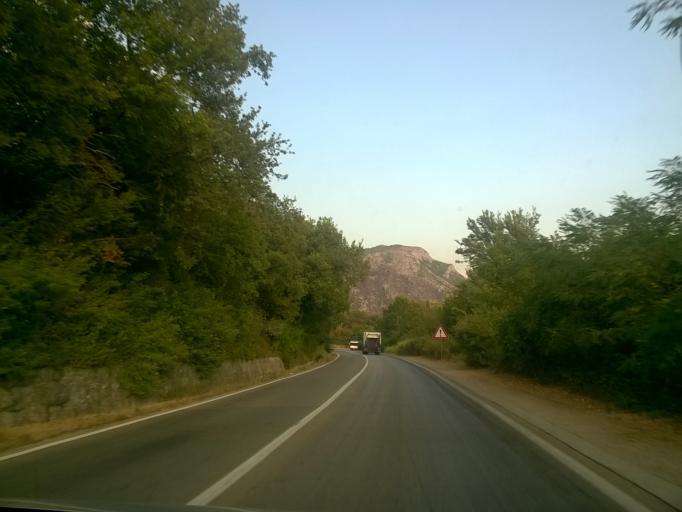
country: ME
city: Petrovac na Moru
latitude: 42.1975
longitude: 18.9700
